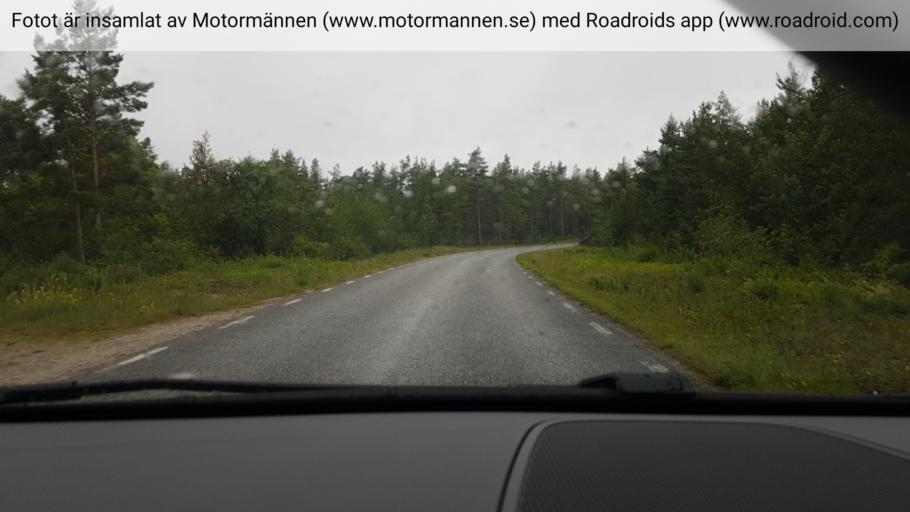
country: SE
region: Gotland
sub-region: Gotland
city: Slite
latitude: 57.8611
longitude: 18.8551
